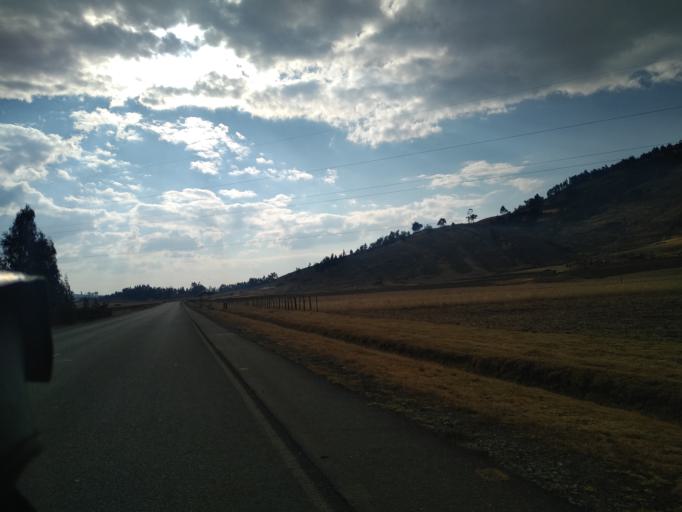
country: PE
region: Cajamarca
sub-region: Provincia de Cajamarca
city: Encanada
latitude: -7.1388
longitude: -78.3832
